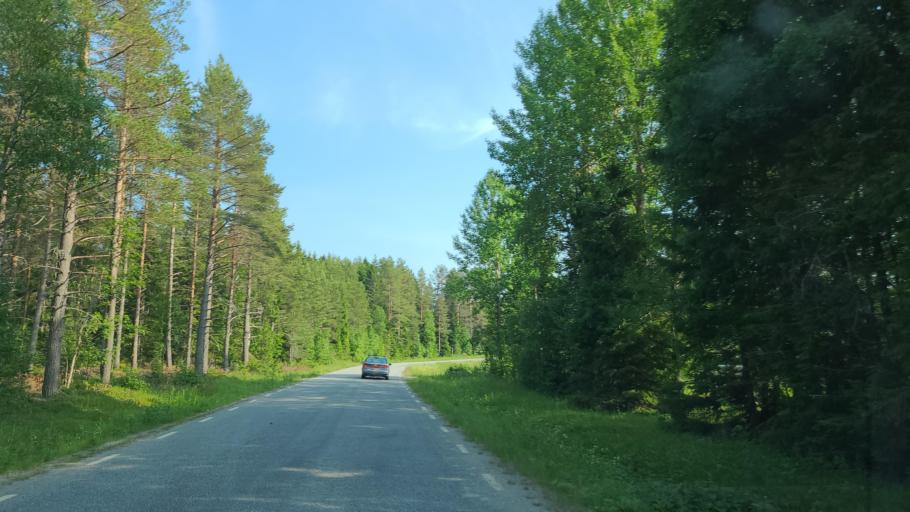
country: SE
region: Vaesterbotten
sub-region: Skelleftea Kommun
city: Burea
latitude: 64.3586
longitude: 21.3367
